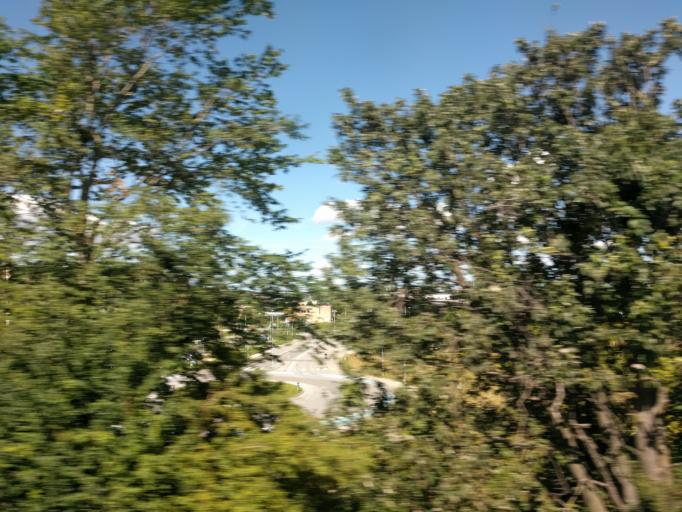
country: DK
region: Zealand
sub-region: Roskilde Kommune
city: Vindinge
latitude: 55.6482
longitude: 12.1376
